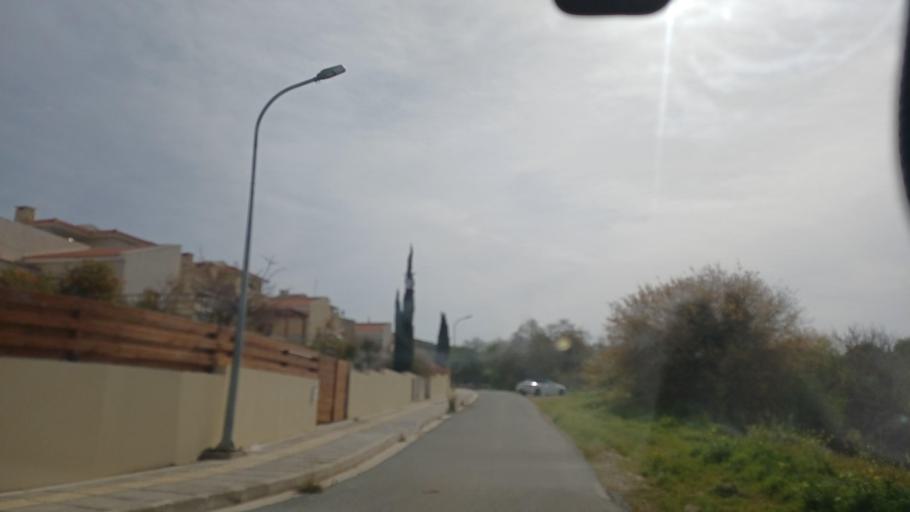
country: CY
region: Pafos
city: Mesogi
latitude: 34.7831
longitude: 32.4674
